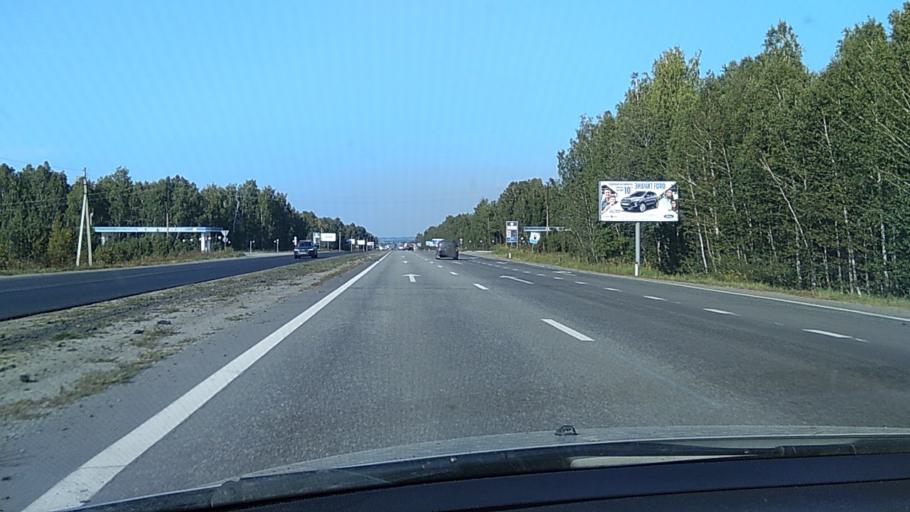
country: RU
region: Chelyabinsk
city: Sargazy
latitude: 55.0249
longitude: 61.2955
